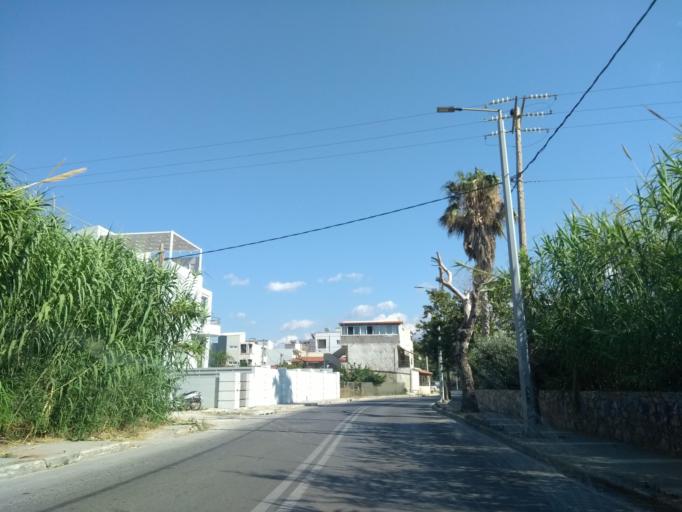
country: GR
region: Crete
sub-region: Nomos Chanias
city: Perivolia
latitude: 35.5105
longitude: 24.0024
